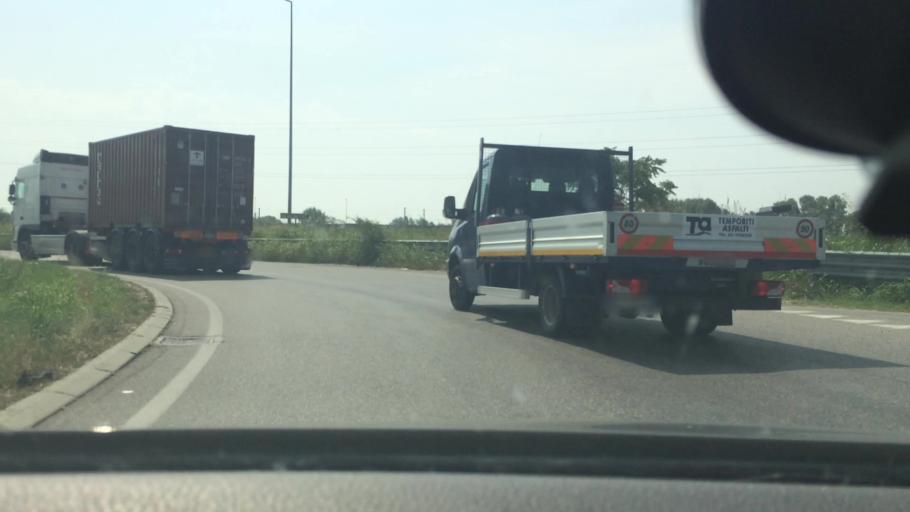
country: IT
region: Lombardy
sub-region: Citta metropolitana di Milano
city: Santo Stefano Ticino
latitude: 45.5001
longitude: 8.9197
